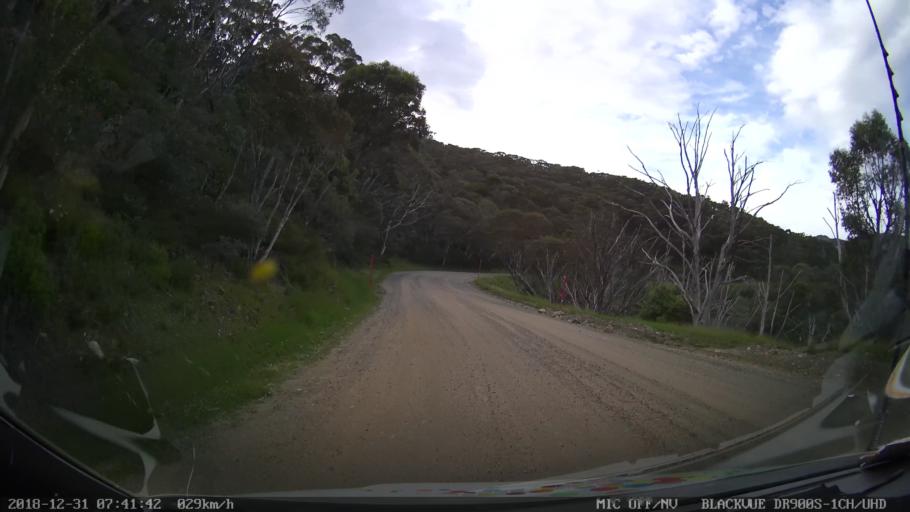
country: AU
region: New South Wales
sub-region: Snowy River
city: Jindabyne
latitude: -36.3542
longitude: 148.4114
